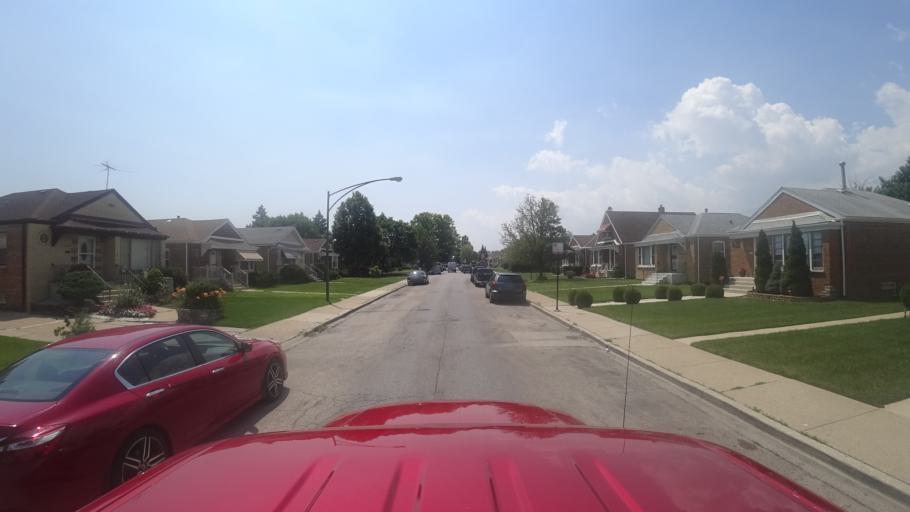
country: US
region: Illinois
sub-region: Cook County
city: Cicero
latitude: 41.7957
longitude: -87.7208
